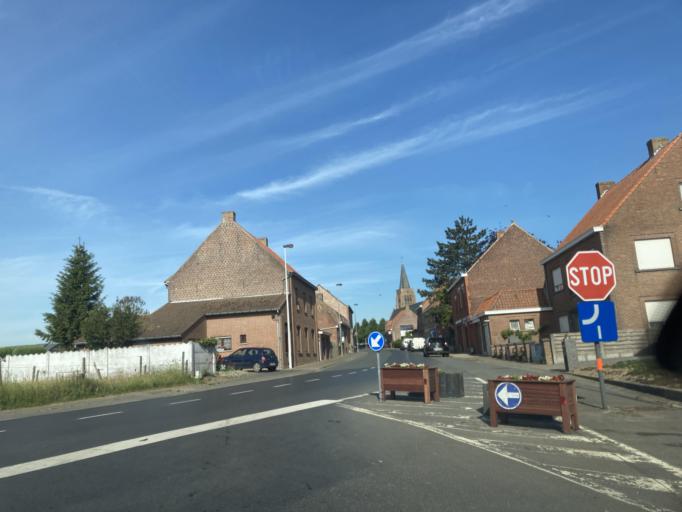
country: FR
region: Nord-Pas-de-Calais
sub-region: Departement du Nord
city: Bailleul
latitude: 50.7659
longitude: 2.7865
